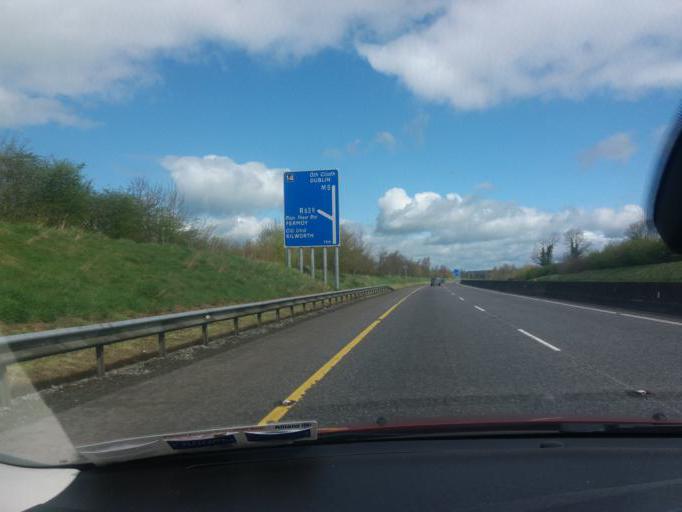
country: IE
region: Munster
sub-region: County Cork
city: Fermoy
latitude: 52.1478
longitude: -8.2659
